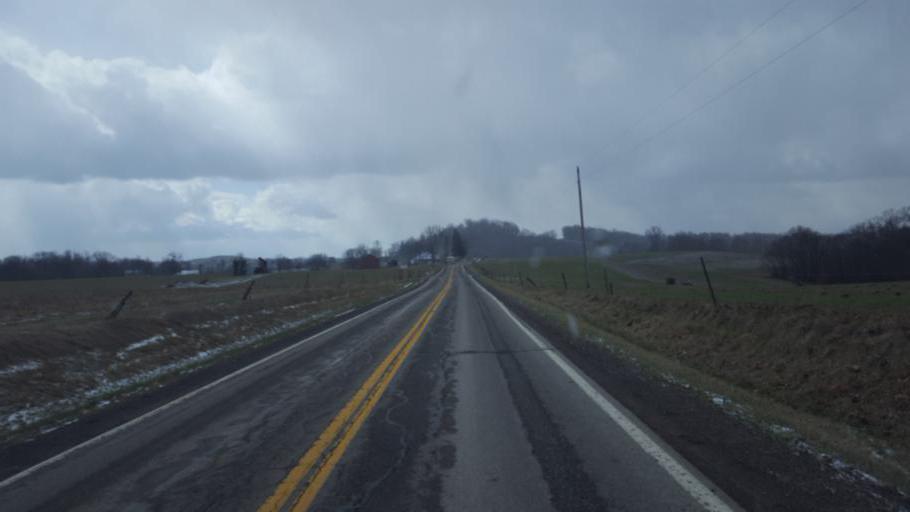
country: US
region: Ohio
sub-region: Coshocton County
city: West Lafayette
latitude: 40.4311
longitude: -81.7854
